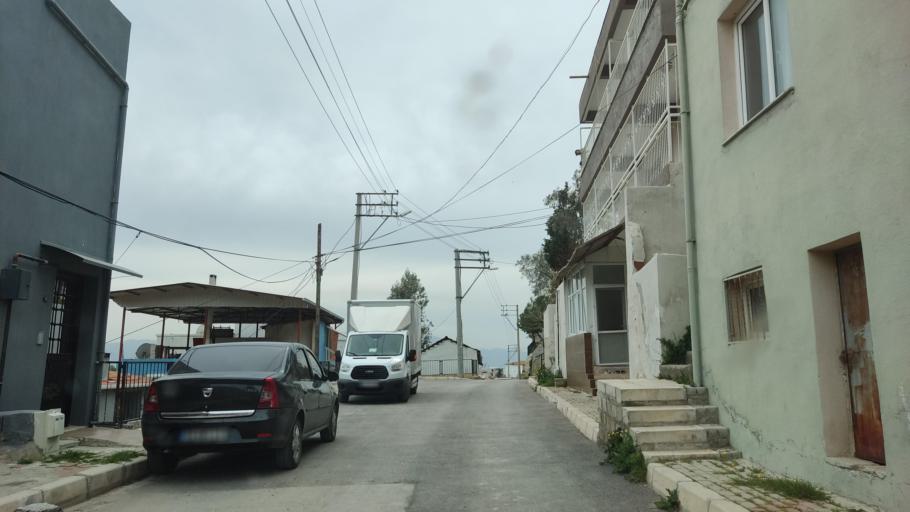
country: TR
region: Izmir
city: Karsiyaka
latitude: 38.4987
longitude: 27.0776
